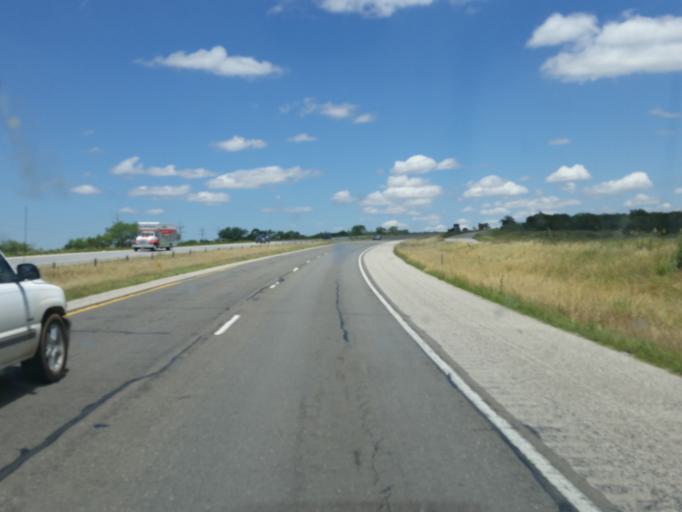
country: US
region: Texas
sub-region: Nolan County
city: Sweetwater
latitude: 32.4962
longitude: -100.2692
